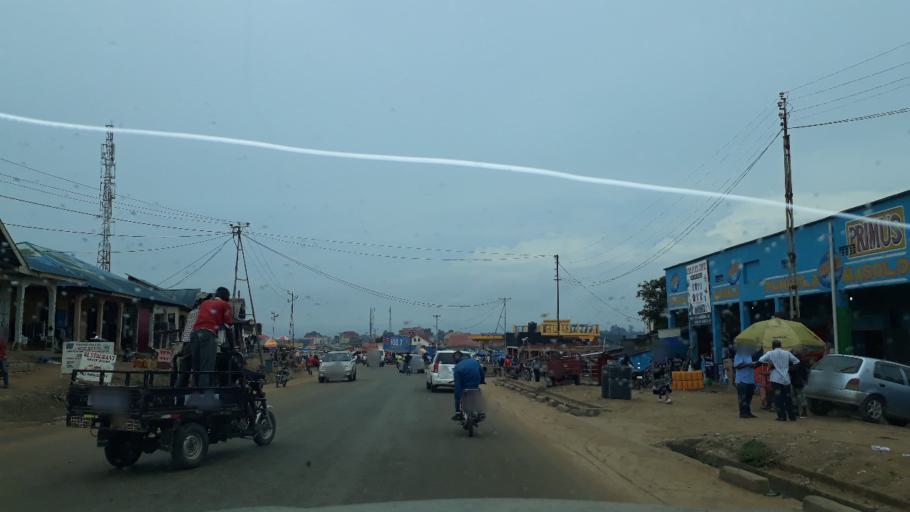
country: CD
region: Eastern Province
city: Bunia
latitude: 1.5656
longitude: 30.2488
